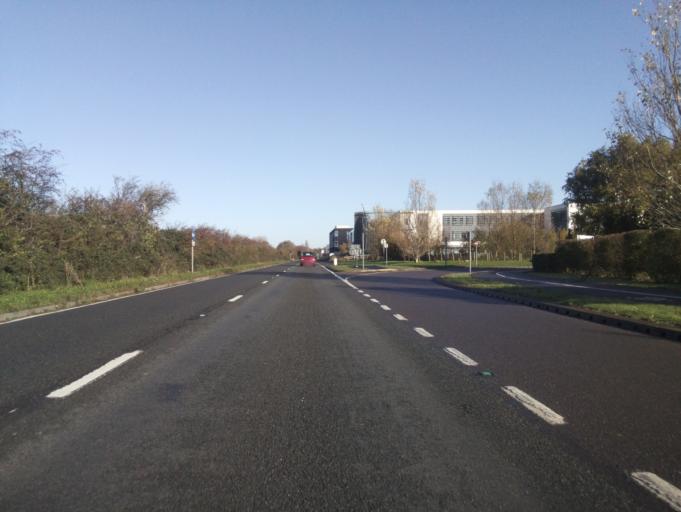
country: GB
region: England
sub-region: Somerset
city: Puriton
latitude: 51.1555
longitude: -2.9874
